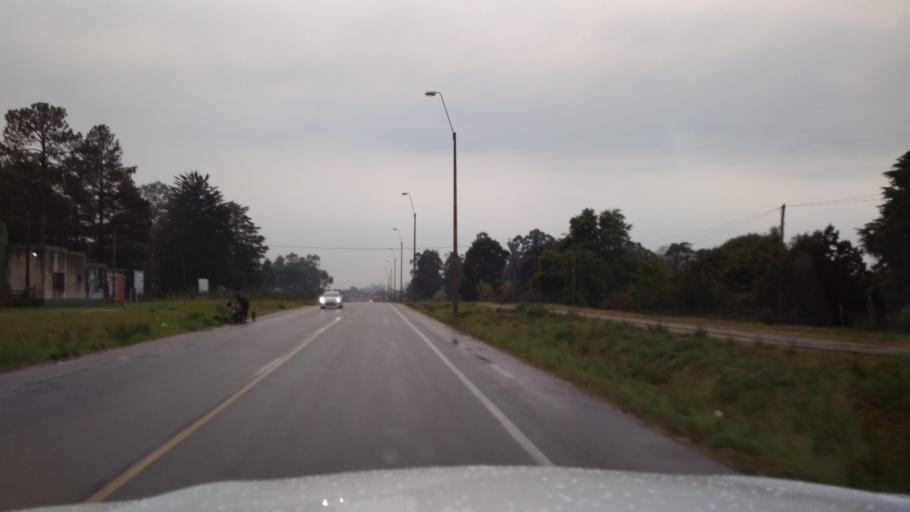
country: UY
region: Canelones
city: Toledo
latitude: -34.7617
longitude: -56.1166
